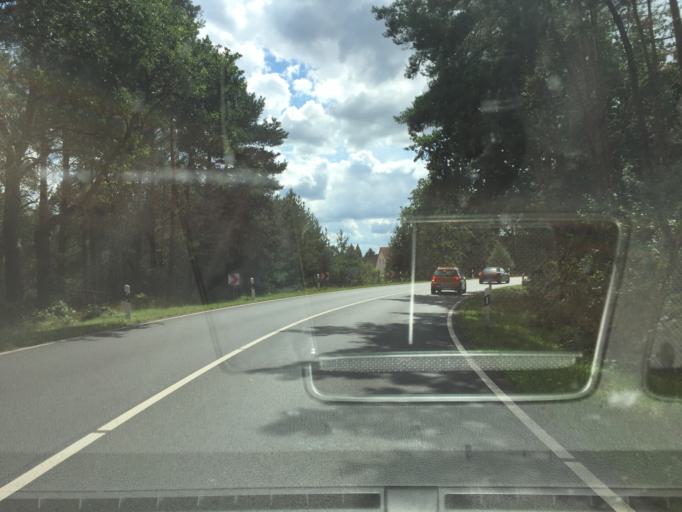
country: DE
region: Lower Saxony
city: Rohrsen
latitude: 52.7001
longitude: 9.2387
